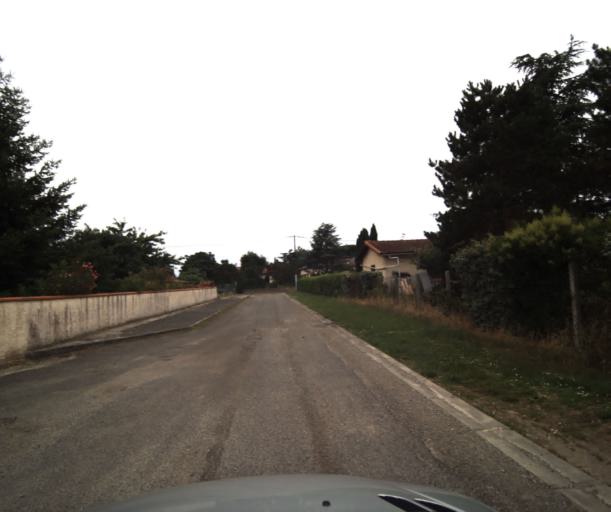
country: FR
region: Midi-Pyrenees
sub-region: Departement de la Haute-Garonne
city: Labarthe-sur-Leze
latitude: 43.4486
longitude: 1.3985
